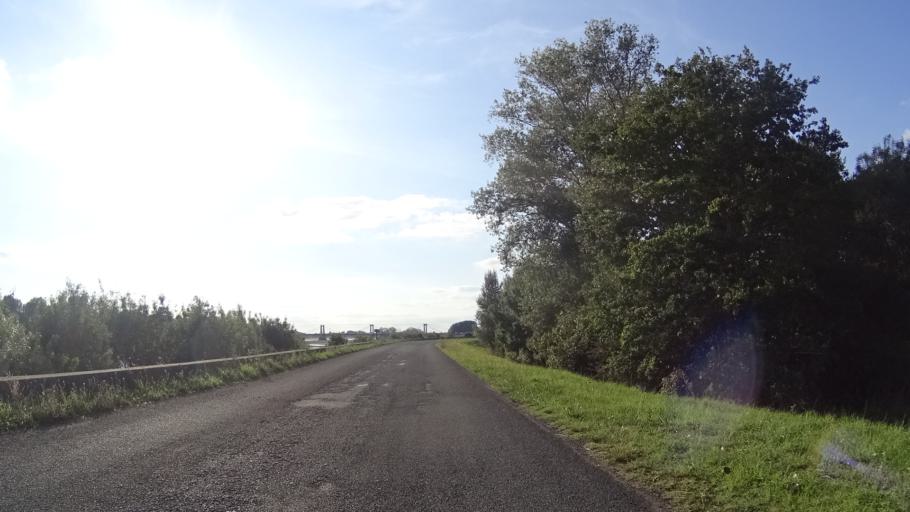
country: FR
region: Pays de la Loire
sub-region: Departement de Maine-et-Loire
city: Montjean-sur-Loire
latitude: 47.3952
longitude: -0.8468
